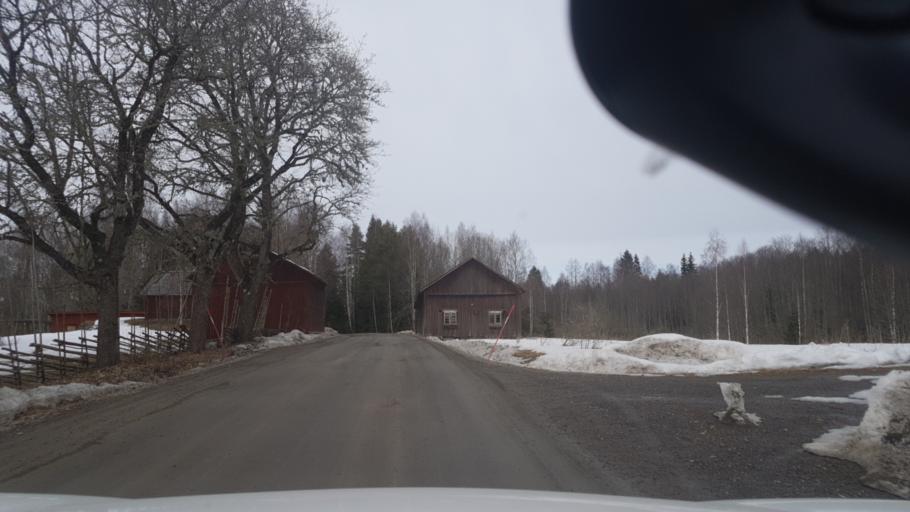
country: SE
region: Vaermland
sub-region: Eda Kommun
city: Amotfors
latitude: 59.7701
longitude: 12.4439
